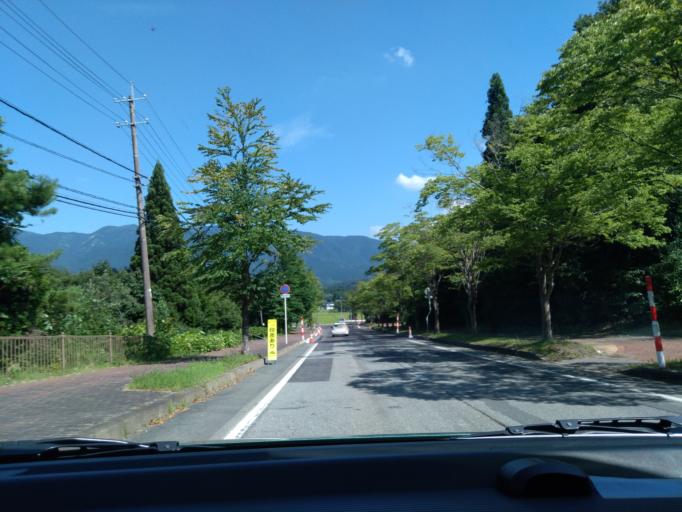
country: JP
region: Akita
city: Kakunodatemachi
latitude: 39.7354
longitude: 140.7039
